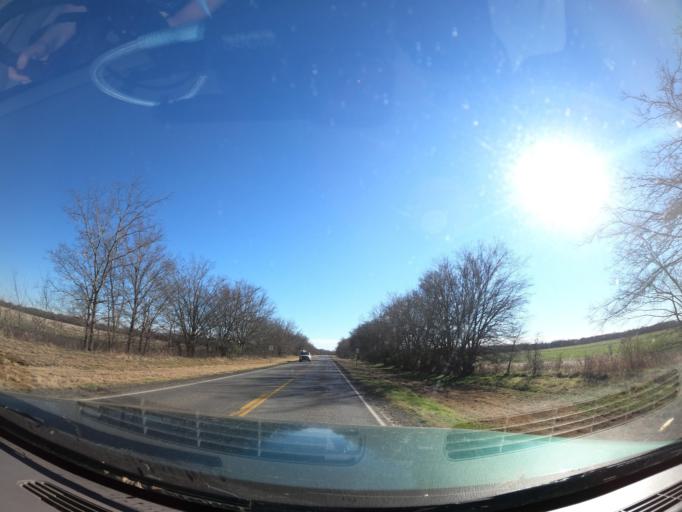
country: US
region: Oklahoma
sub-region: McIntosh County
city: Checotah
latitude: 35.5654
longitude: -95.6542
